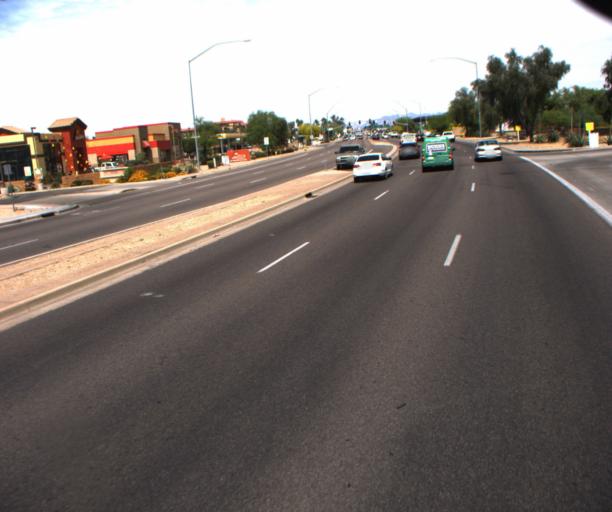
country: US
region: Arizona
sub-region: Maricopa County
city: San Carlos
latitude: 33.3802
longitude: -111.8402
